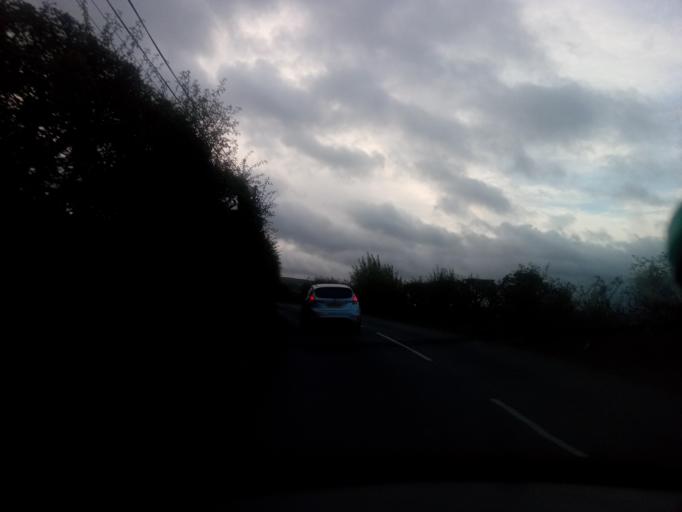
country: GB
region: Scotland
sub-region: The Scottish Borders
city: Jedburgh
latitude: 55.3940
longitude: -2.6493
